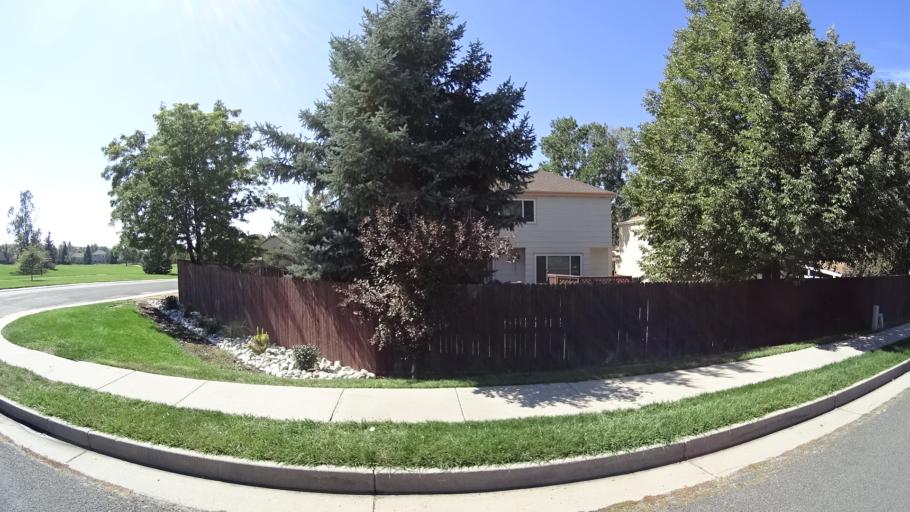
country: US
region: Colorado
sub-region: El Paso County
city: Cimarron Hills
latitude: 38.9003
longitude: -104.7005
